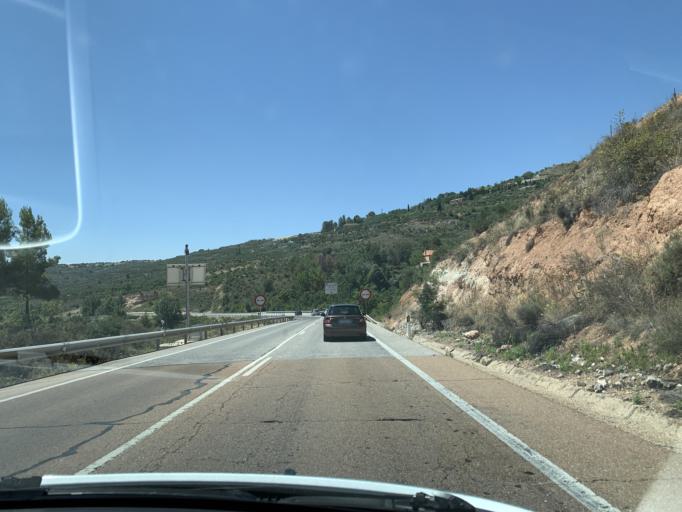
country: ES
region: Castille-La Mancha
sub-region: Provincia de Guadalajara
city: Horche
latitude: 40.5733
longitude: -3.0528
